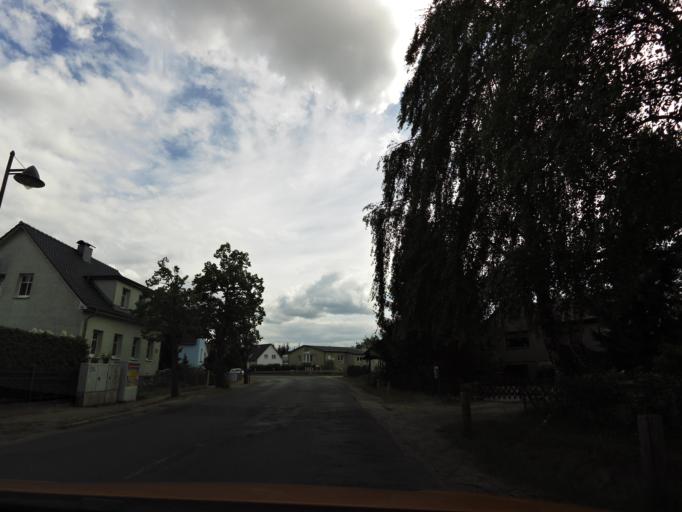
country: DE
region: Brandenburg
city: Michendorf
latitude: 52.3204
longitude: 13.1216
